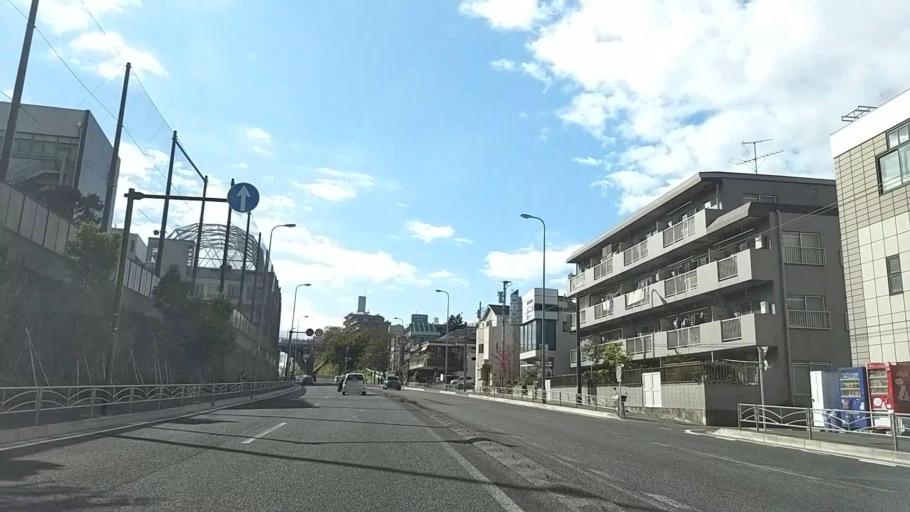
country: JP
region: Kanagawa
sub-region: Kawasaki-shi
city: Kawasaki
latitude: 35.5140
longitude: 139.6643
